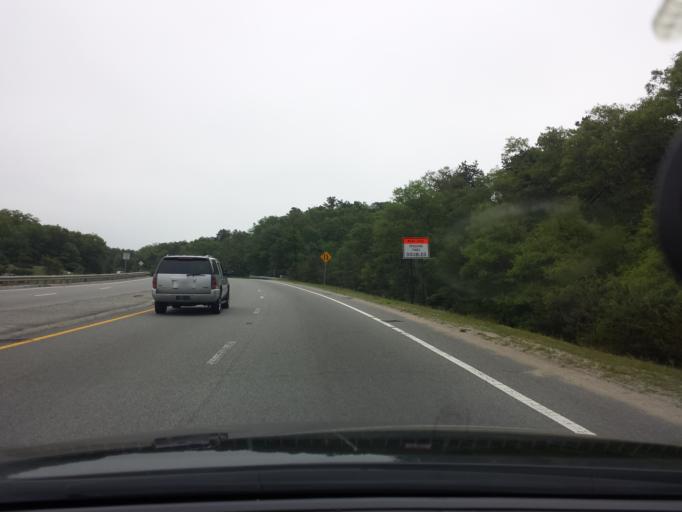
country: US
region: Massachusetts
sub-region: Barnstable County
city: Sagamore
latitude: 41.7711
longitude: -70.5474
